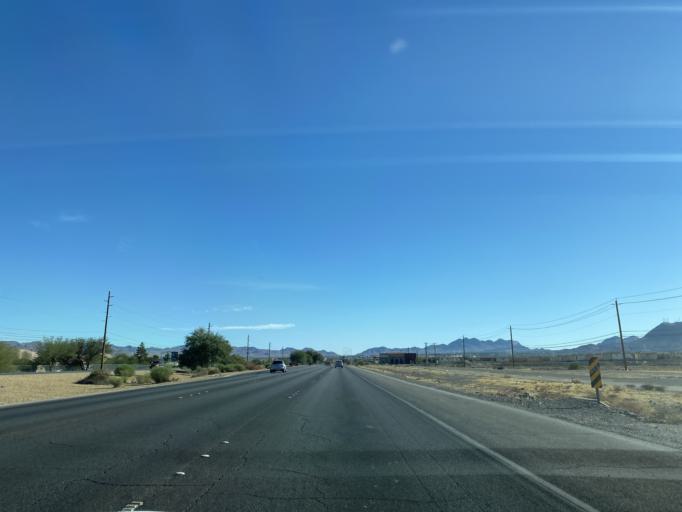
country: US
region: Nevada
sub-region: Clark County
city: Henderson
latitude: 36.0743
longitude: -115.0213
